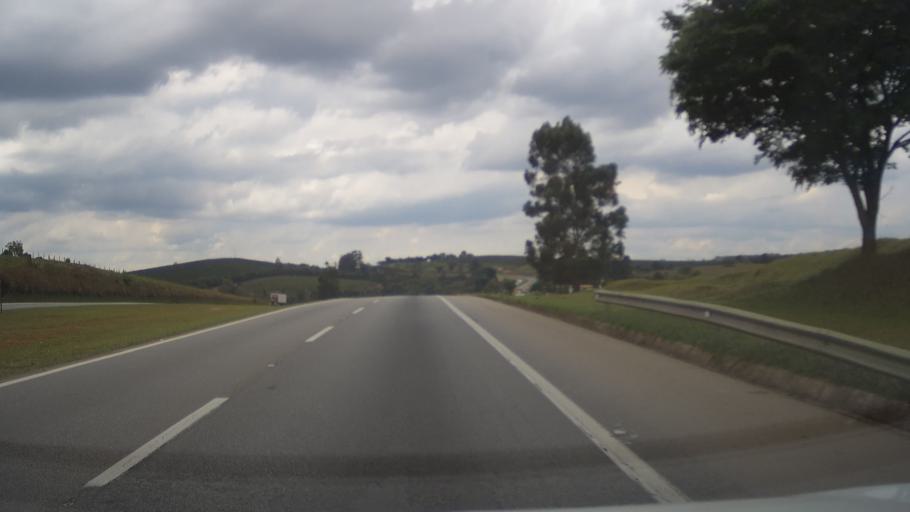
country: BR
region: Minas Gerais
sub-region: Tres Coracoes
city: Tres Coracoes
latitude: -21.4876
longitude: -45.2064
